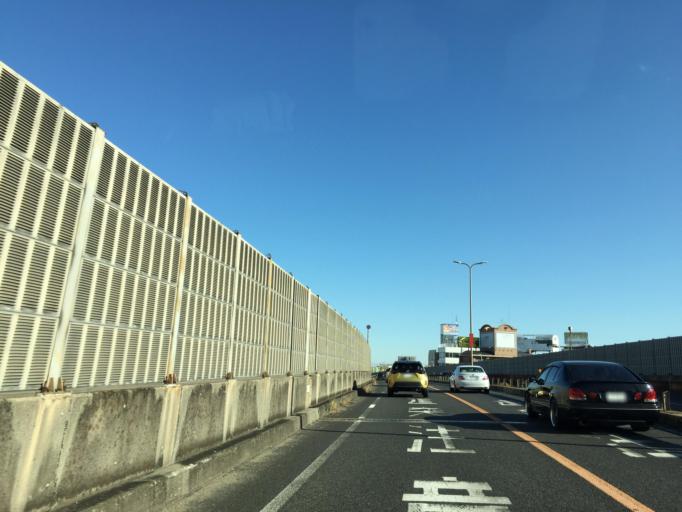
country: JP
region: Osaka
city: Kaizuka
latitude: 34.4145
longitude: 135.3350
